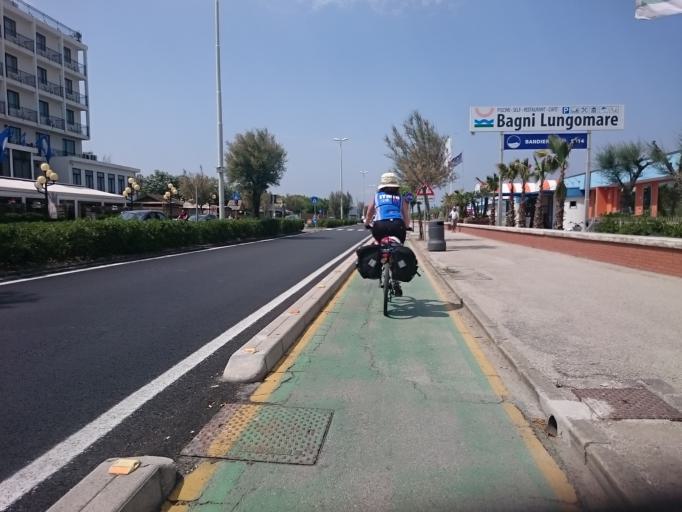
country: IT
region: Veneto
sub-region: Provincia di Venezia
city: Chioggia
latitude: 45.2029
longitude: 12.3001
